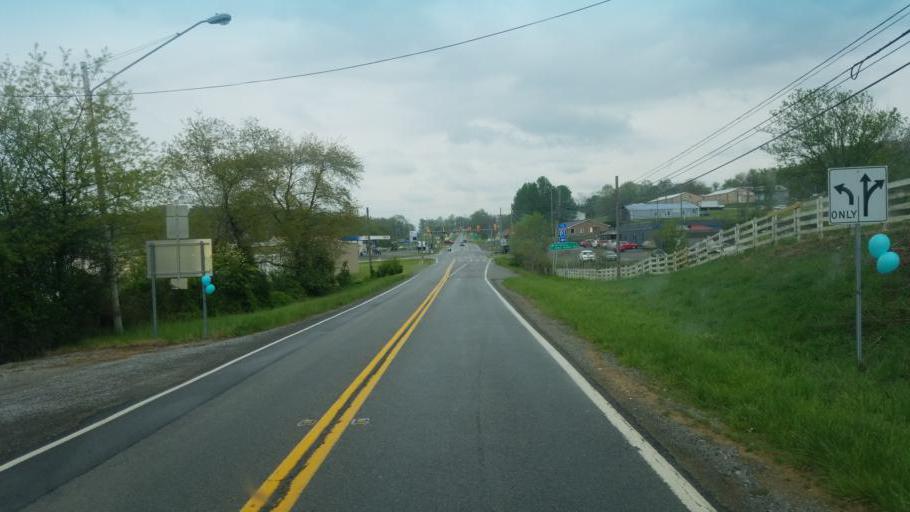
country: US
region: Virginia
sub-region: Wythe County
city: Rural Retreat
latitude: 36.9097
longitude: -81.2756
